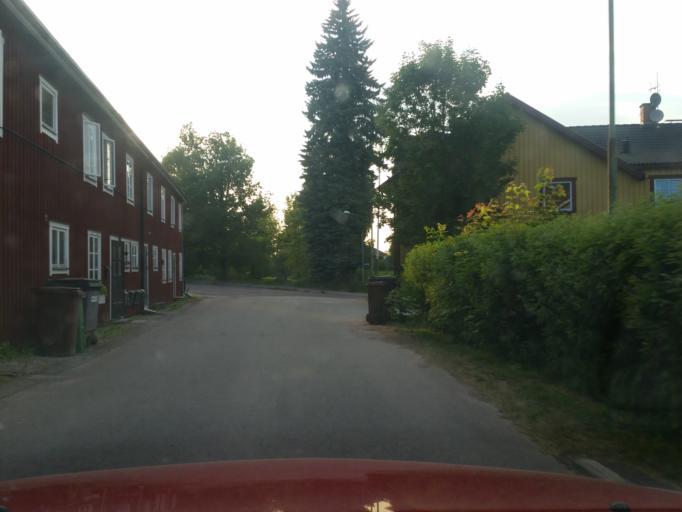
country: SE
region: Dalarna
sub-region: Leksand Municipality
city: Smedby
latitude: 60.6794
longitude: 15.1025
